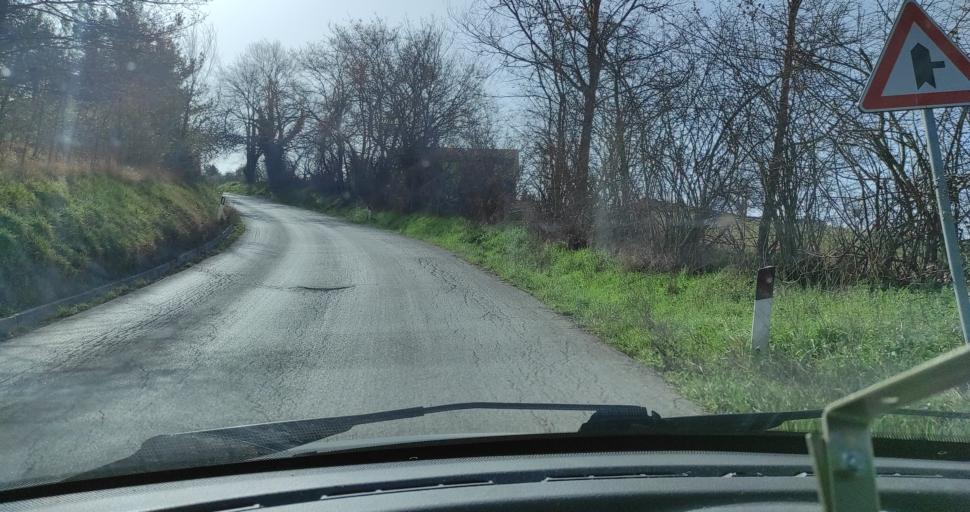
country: IT
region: The Marches
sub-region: Provincia di Macerata
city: Loro Piceno
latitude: 43.1723
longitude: 13.3964
